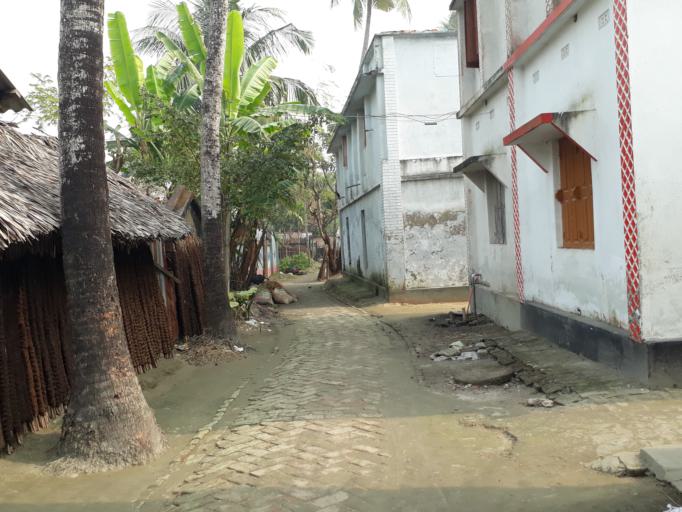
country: BD
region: Khulna
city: Kesabpur
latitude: 22.7903
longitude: 89.2741
